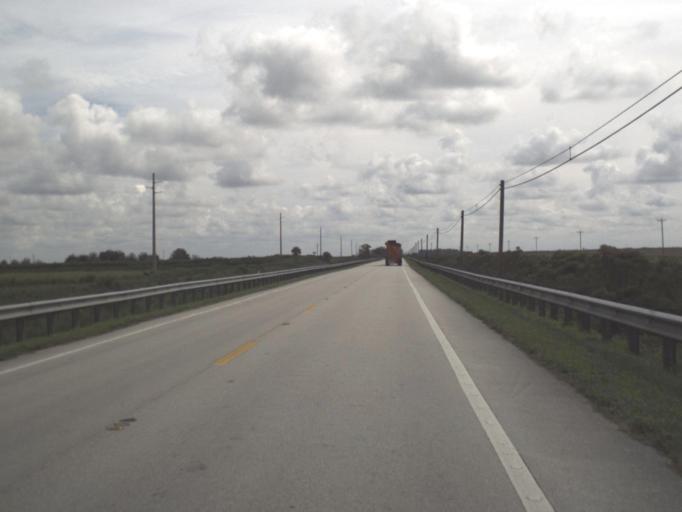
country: US
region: Florida
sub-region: Highlands County
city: Lake Placid
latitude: 27.2085
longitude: -81.2547
